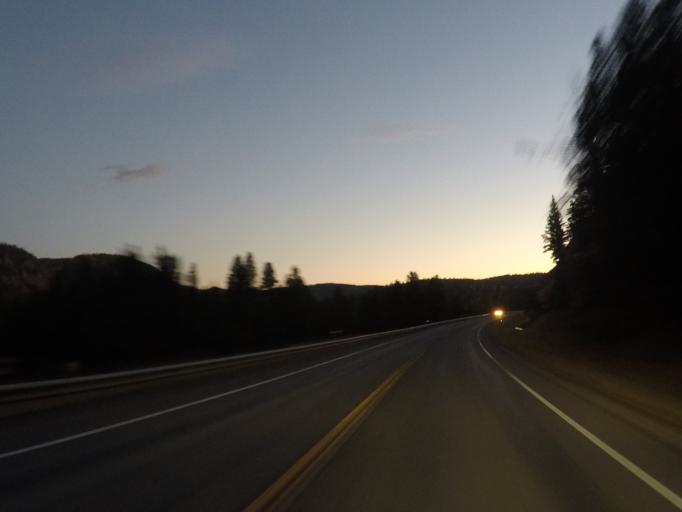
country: US
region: Montana
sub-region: Missoula County
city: Seeley Lake
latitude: 47.0162
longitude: -113.3210
